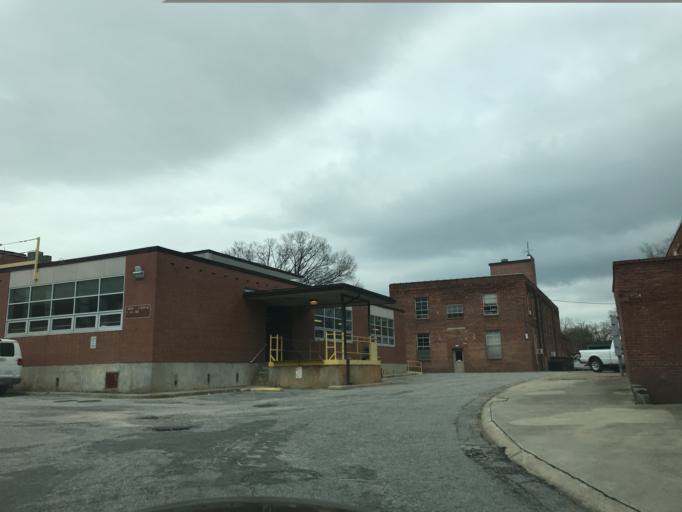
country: US
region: North Carolina
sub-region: Wake County
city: Raleigh
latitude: 35.7689
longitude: -78.6568
